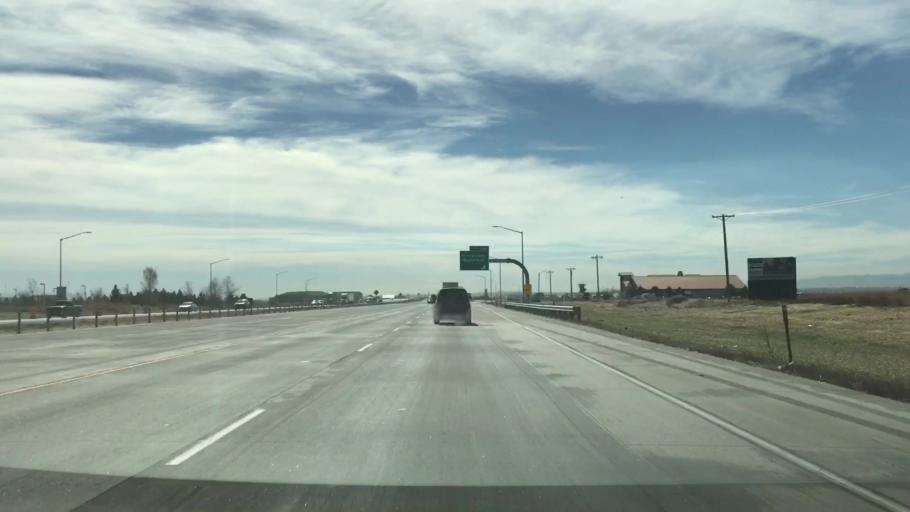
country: US
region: Colorado
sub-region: Larimer County
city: Loveland
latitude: 40.4424
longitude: -104.9925
